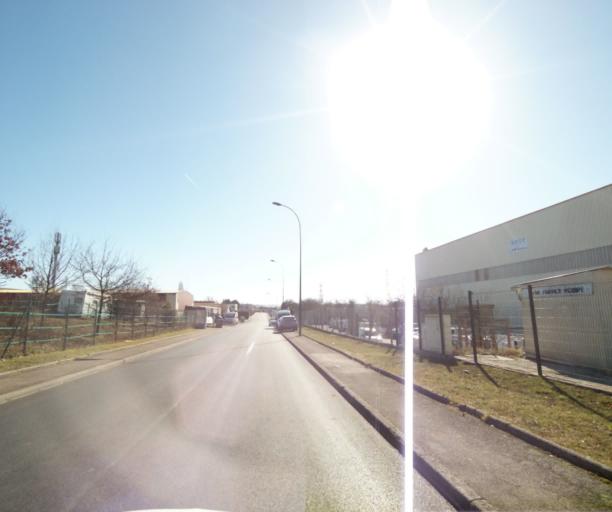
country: FR
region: Lorraine
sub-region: Departement de Meurthe-et-Moselle
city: Heillecourt
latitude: 48.6514
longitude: 6.2091
